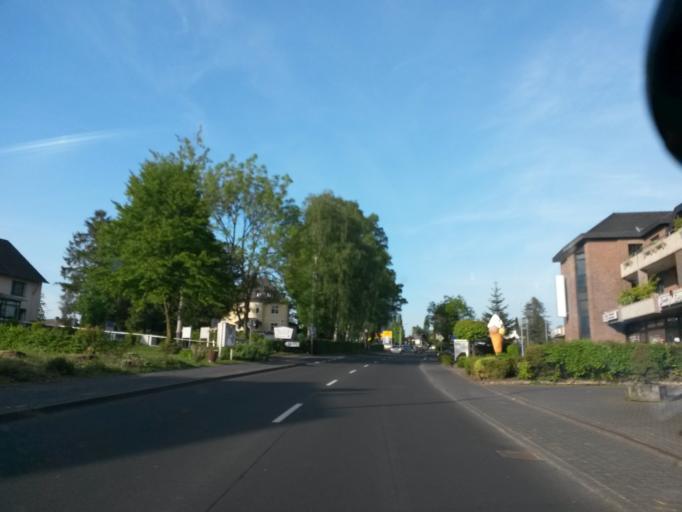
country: DE
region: North Rhine-Westphalia
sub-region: Regierungsbezirk Koln
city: Overath
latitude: 50.8723
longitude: 7.3261
